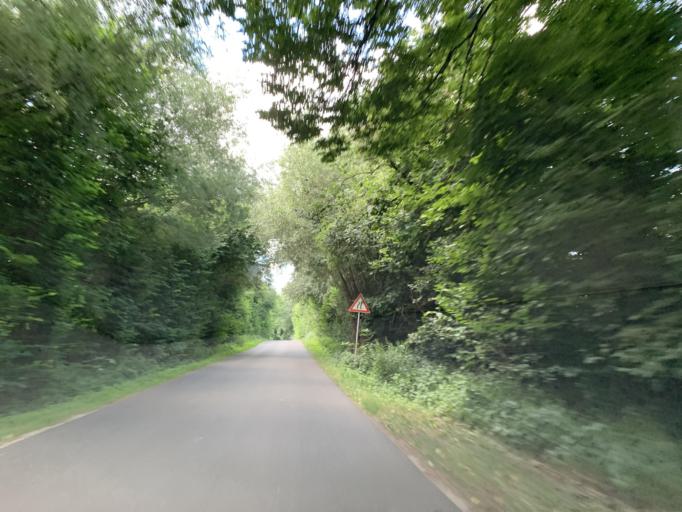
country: DE
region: Mecklenburg-Vorpommern
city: Carpin
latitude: 53.3697
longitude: 13.2565
